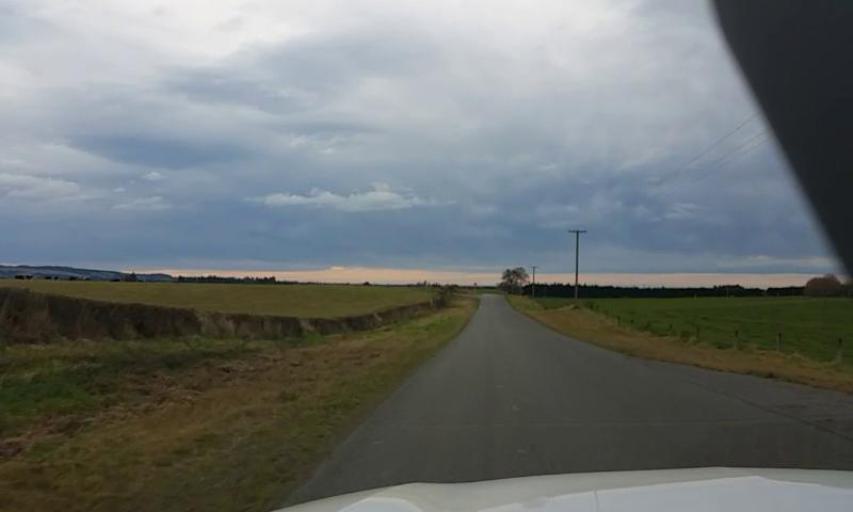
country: NZ
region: Canterbury
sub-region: Waimakariri District
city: Kaiapoi
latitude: -43.2910
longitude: 172.4651
